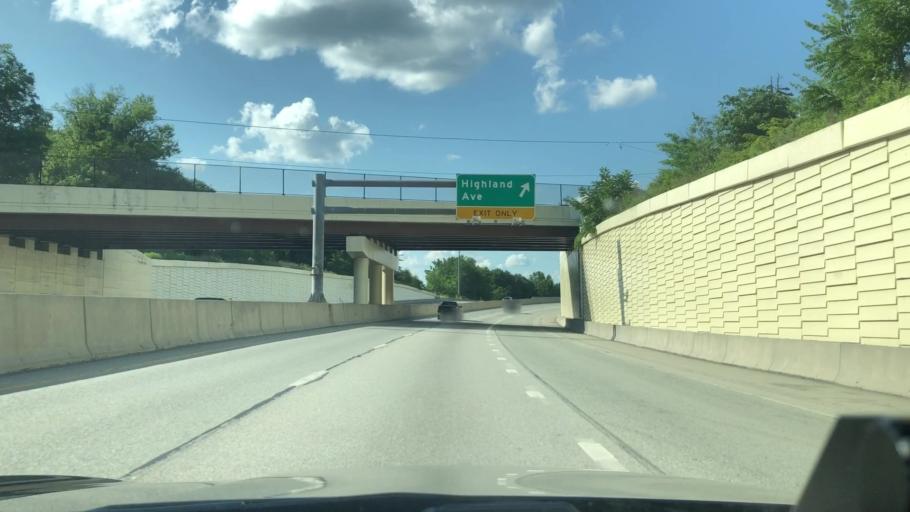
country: US
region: Pennsylvania
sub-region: Montgomery County
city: Fort Washington
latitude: 40.1443
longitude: -75.2040
